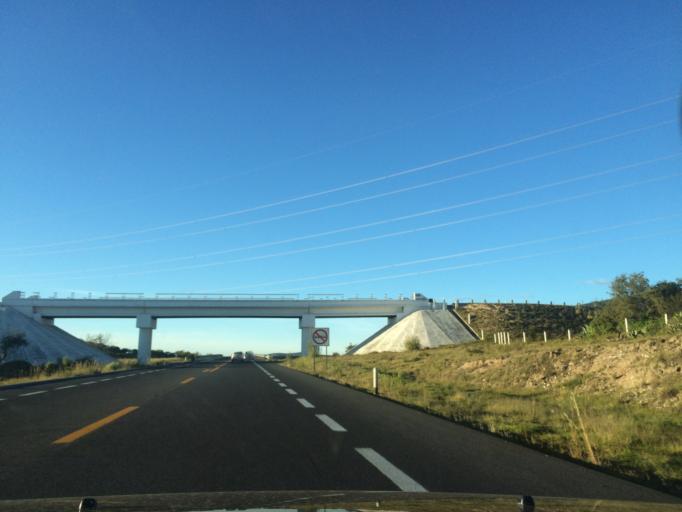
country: MX
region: Puebla
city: Morelos Canada
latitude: 18.7037
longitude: -97.4668
